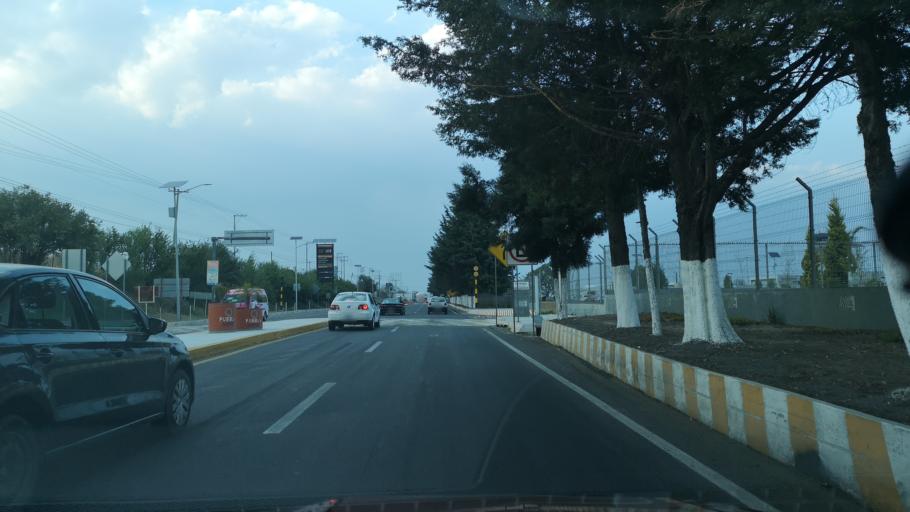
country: MX
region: Puebla
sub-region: Huejotzingo
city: Los Encinos
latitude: 19.1626
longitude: -98.3773
